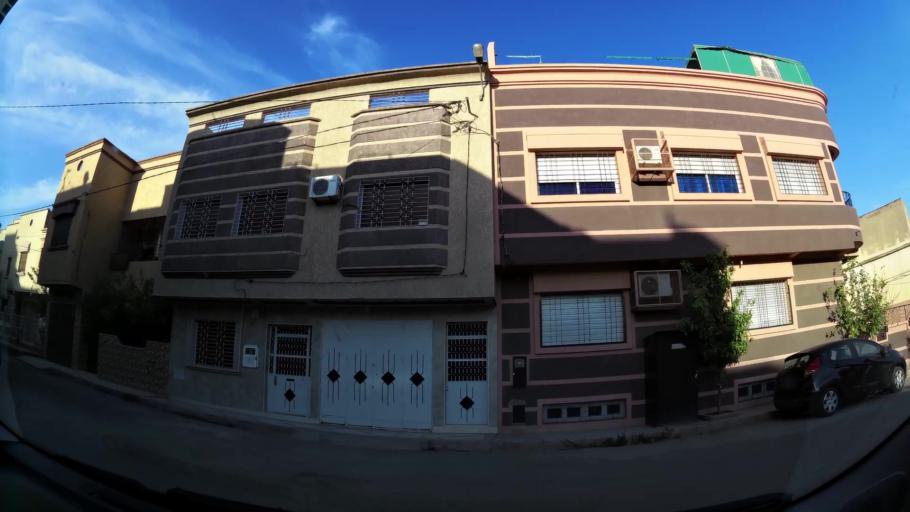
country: MA
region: Oriental
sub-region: Oujda-Angad
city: Oujda
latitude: 34.7009
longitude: -1.9133
